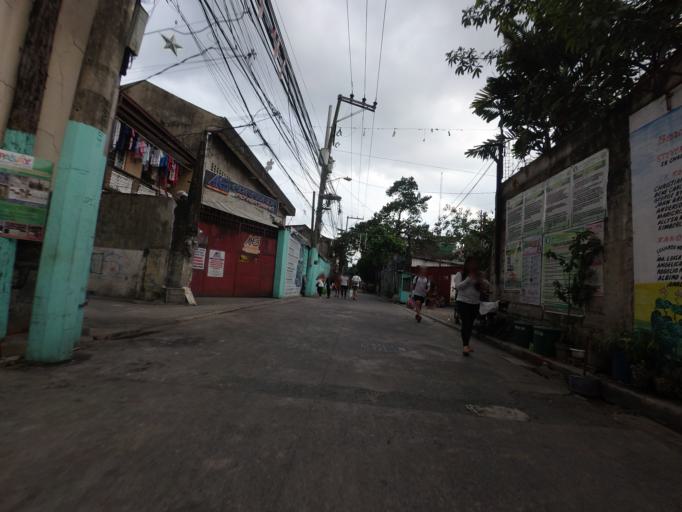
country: PH
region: Metro Manila
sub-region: City of Manila
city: Port Area
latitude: 14.5558
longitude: 120.9940
